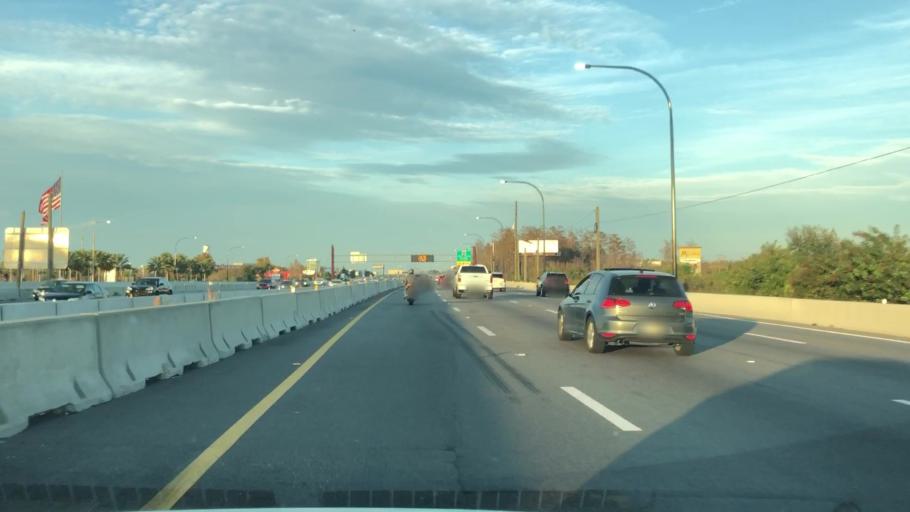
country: US
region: Florida
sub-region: Orange County
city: Oak Ridge
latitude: 28.5003
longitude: -81.4265
